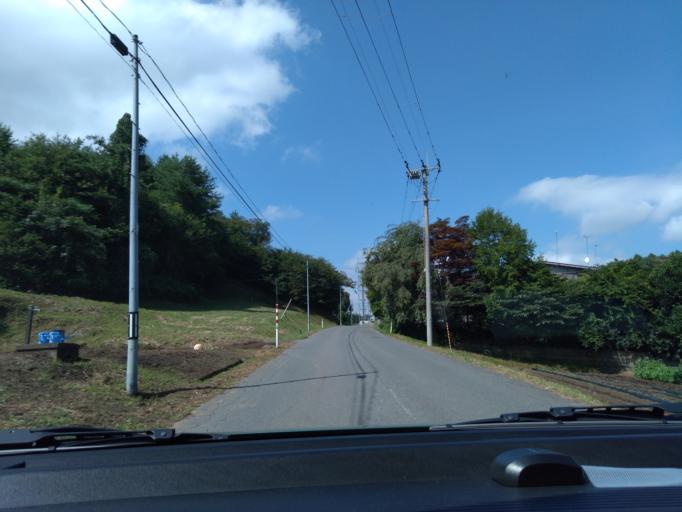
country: JP
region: Iwate
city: Shizukuishi
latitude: 39.6697
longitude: 140.9690
